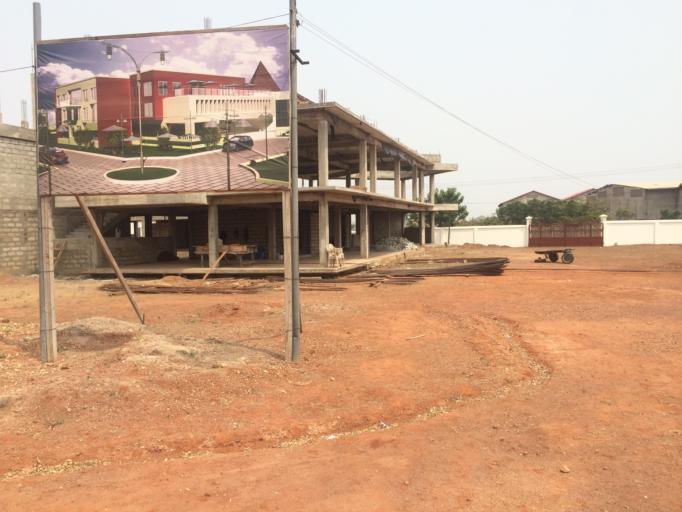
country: GH
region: Greater Accra
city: Nungua
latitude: 5.6532
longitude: -0.0924
